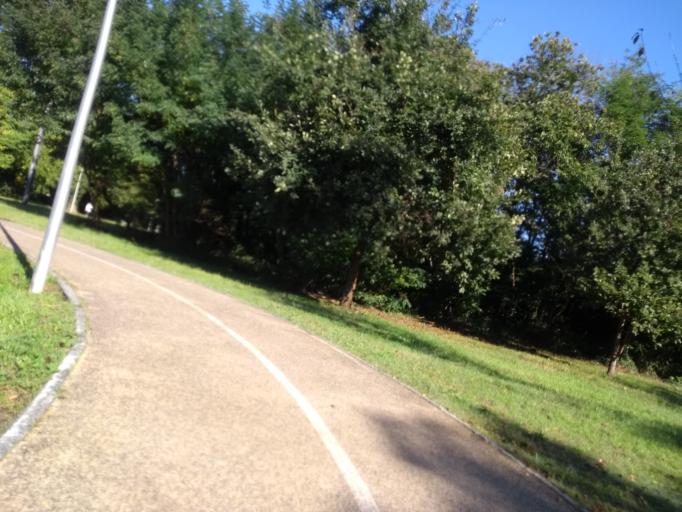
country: FR
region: Aquitaine
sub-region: Departement de la Gironde
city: Pessac
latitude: 44.7981
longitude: -0.6345
